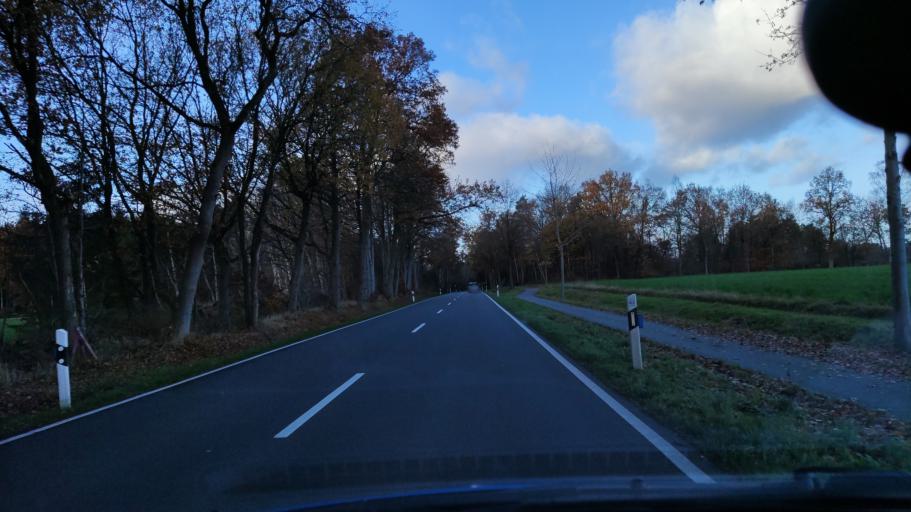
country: DE
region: Lower Saxony
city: Schneverdingen
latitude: 53.0718
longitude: 9.8147
